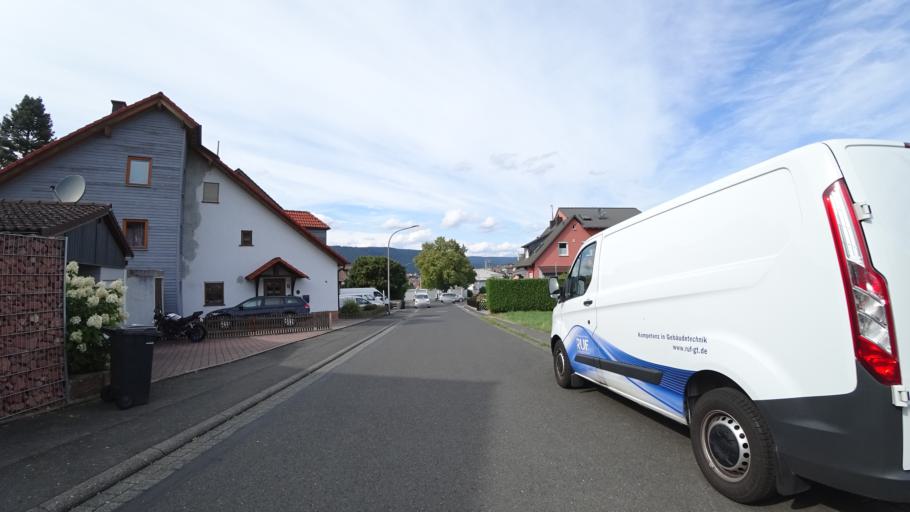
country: DE
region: Bavaria
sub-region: Regierungsbezirk Unterfranken
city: Miltenberg
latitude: 49.7040
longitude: 9.2721
